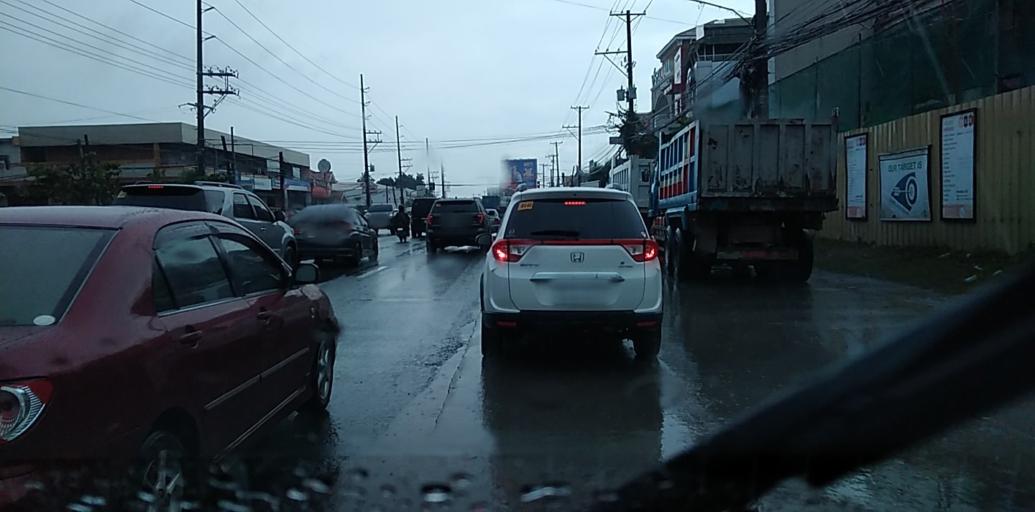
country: PH
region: Central Luzon
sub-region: Province of Pampanga
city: Magliman
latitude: 15.0507
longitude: 120.6645
